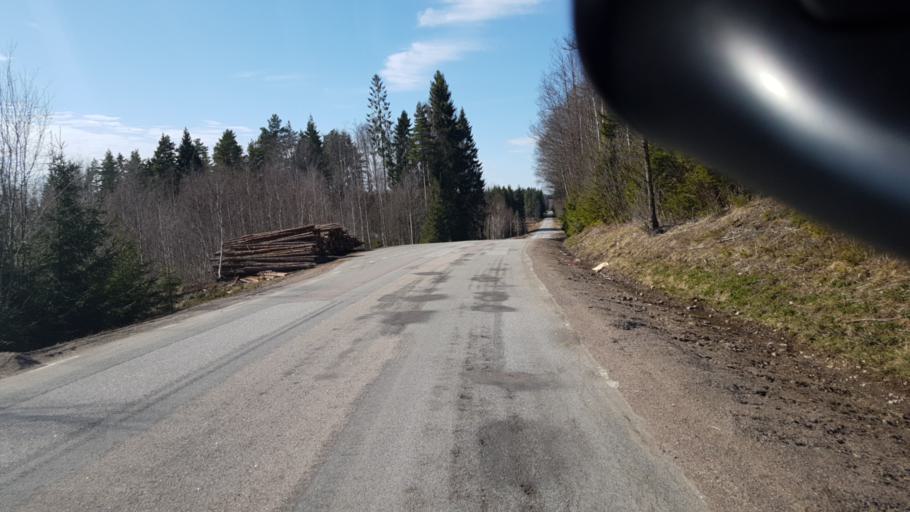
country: SE
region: Vaermland
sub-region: Arvika Kommun
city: Arvika
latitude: 59.6502
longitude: 12.7397
